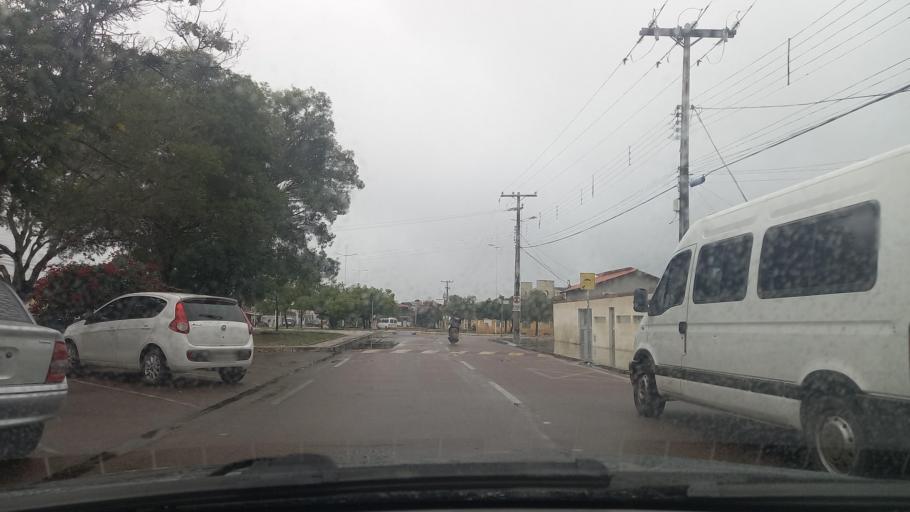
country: BR
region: Bahia
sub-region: Paulo Afonso
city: Paulo Afonso
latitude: -9.4048
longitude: -38.2262
